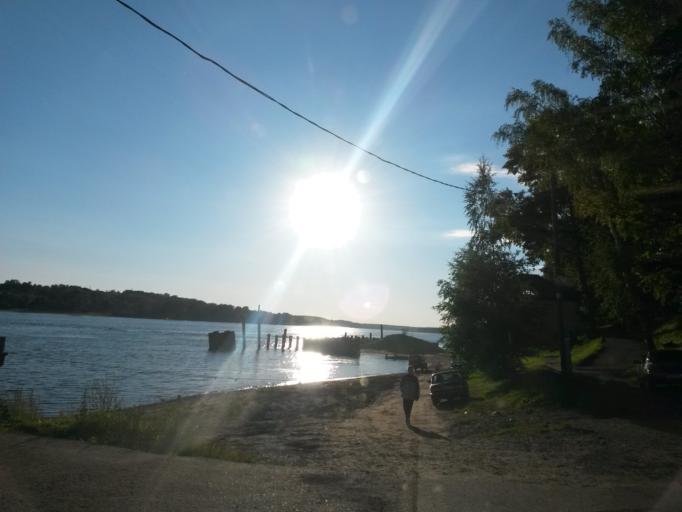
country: RU
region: Jaroslavl
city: Tutayev
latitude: 57.8780
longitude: 39.5408
